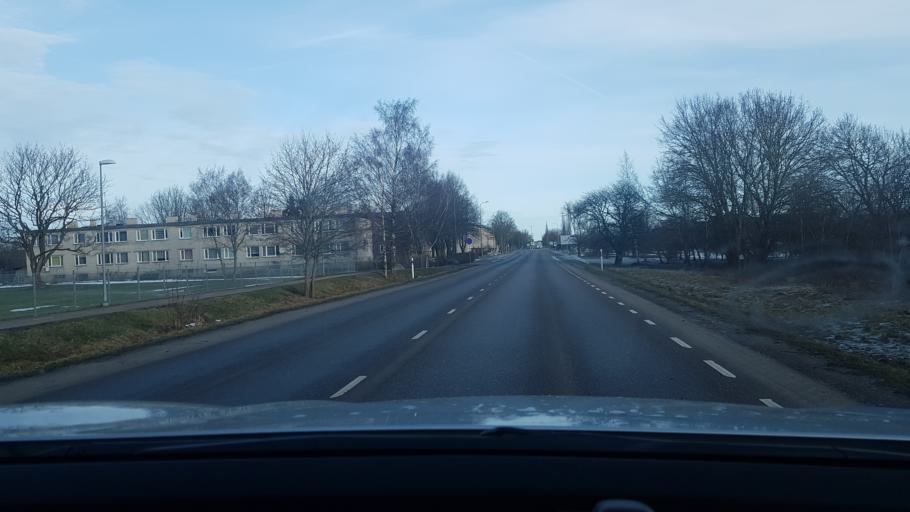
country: EE
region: Saare
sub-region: Kuressaare linn
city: Kuressaare
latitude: 58.2515
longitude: 22.5084
